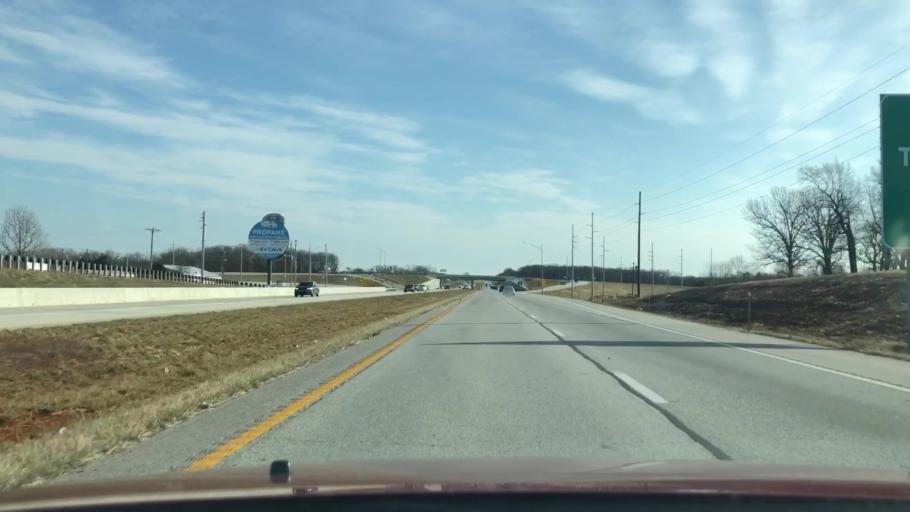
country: US
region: Missouri
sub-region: Christian County
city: Ozark
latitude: 37.1203
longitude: -93.1933
